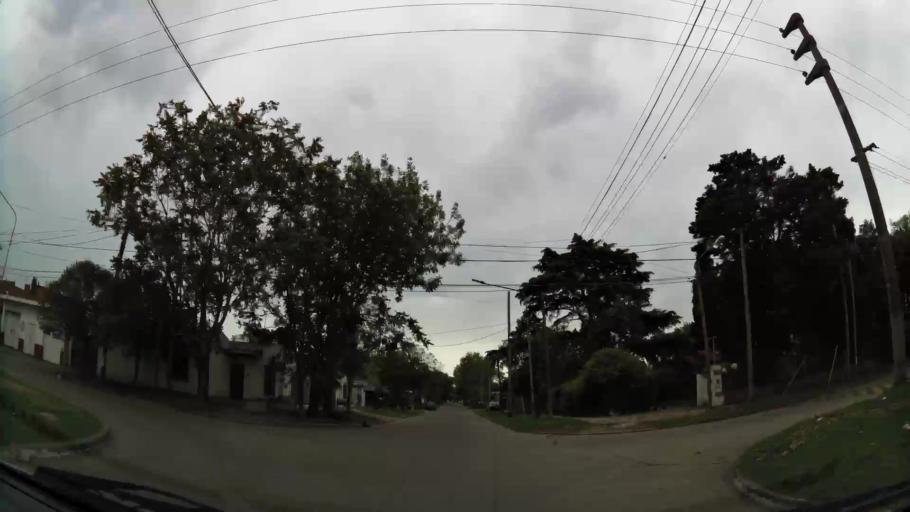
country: AR
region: Buenos Aires
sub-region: Partido de Quilmes
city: Quilmes
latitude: -34.8066
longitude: -58.2701
